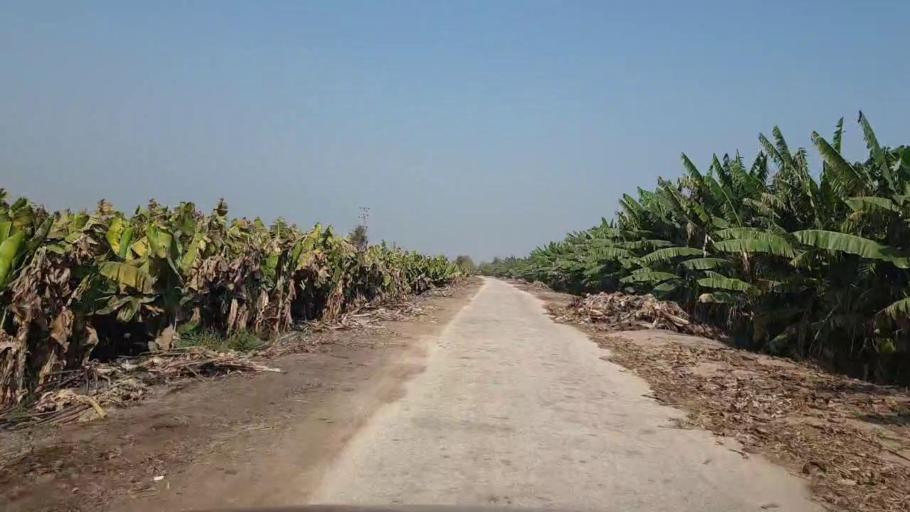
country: PK
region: Sindh
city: Bhit Shah
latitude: 25.7647
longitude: 68.4946
